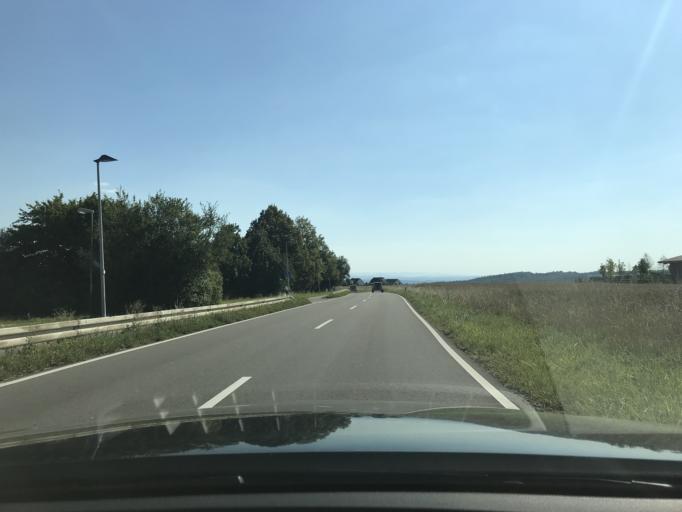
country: DE
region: Baden-Wuerttemberg
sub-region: Regierungsbezirk Stuttgart
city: Baltmannsweiler
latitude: 48.7435
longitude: 9.4822
